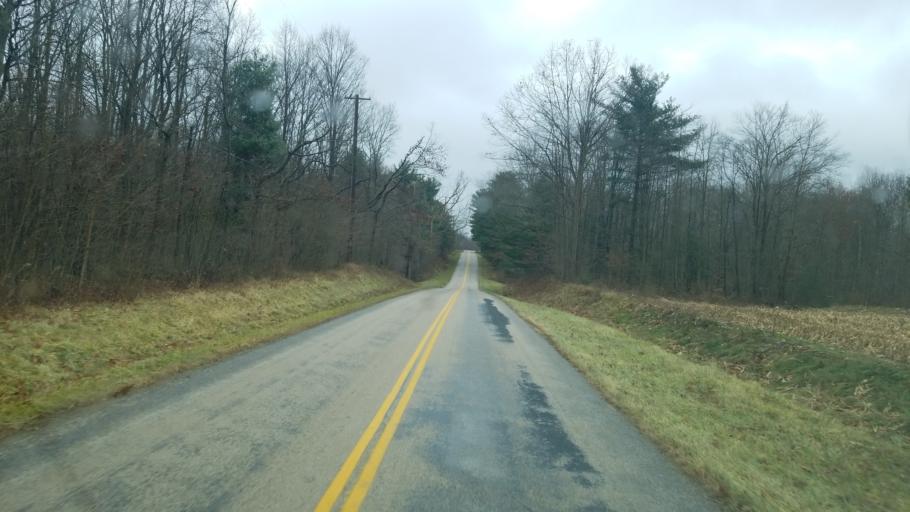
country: US
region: Ohio
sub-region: Ashtabula County
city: Roaming Shores
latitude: 41.7260
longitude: -80.8746
